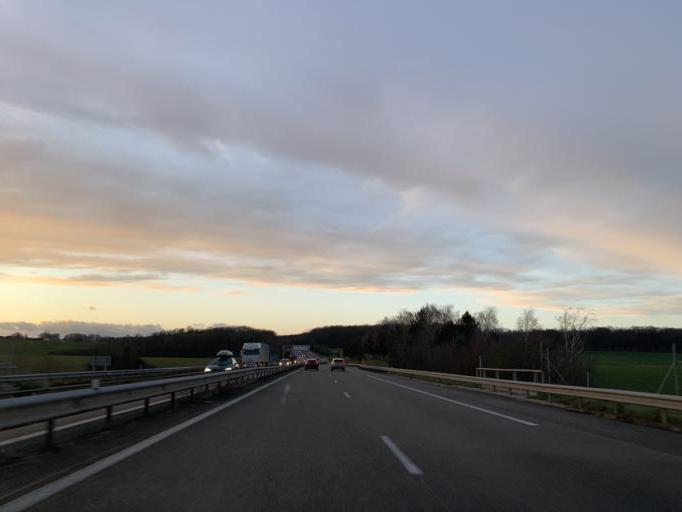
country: FR
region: Champagne-Ardenne
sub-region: Departement de l'Aube
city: Vendeuvre-sur-Barse
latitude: 48.1816
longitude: 4.4204
